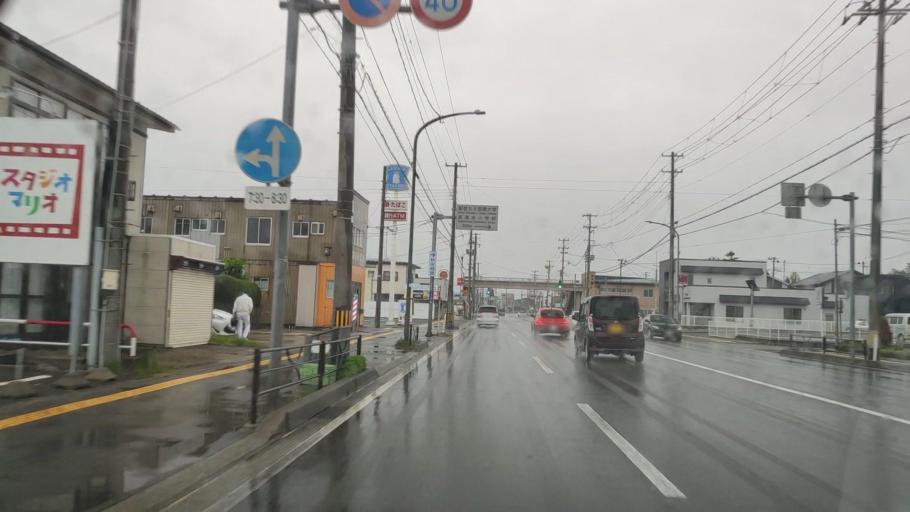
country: JP
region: Akita
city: Akita Shi
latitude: 39.7467
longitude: 140.0832
